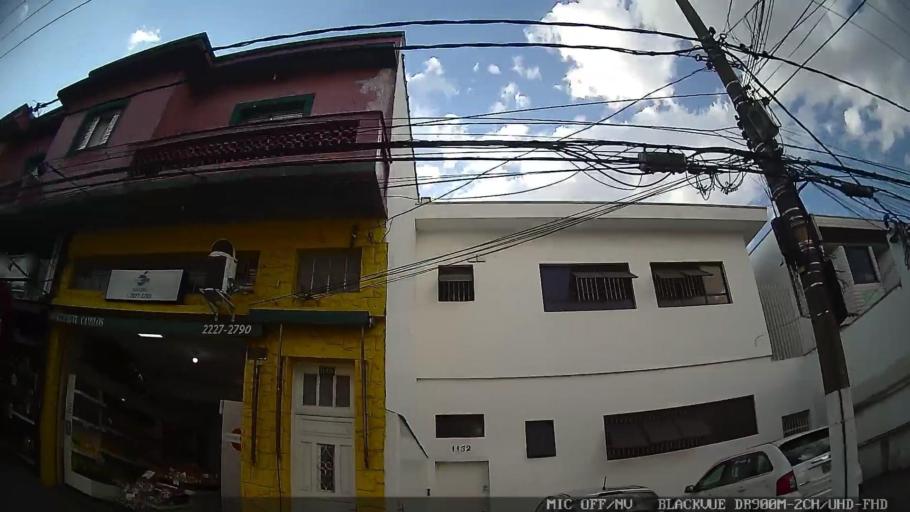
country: BR
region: Sao Paulo
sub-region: Sao Caetano Do Sul
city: Sao Caetano do Sul
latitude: -23.5517
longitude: -46.5514
